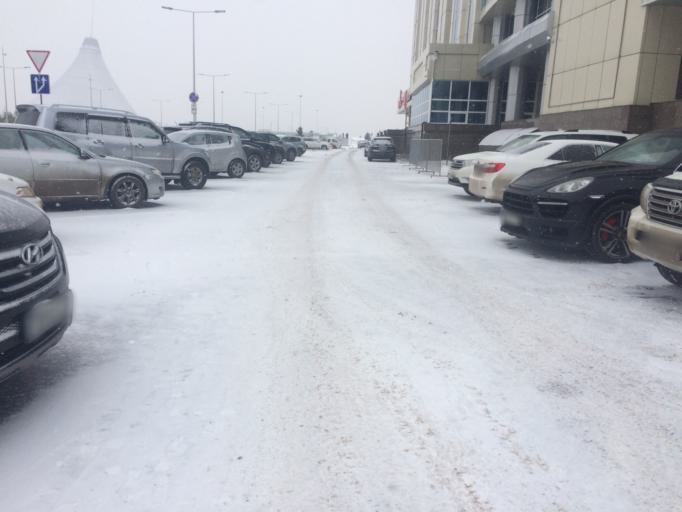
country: KZ
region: Astana Qalasy
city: Astana
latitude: 51.1337
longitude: 71.4137
